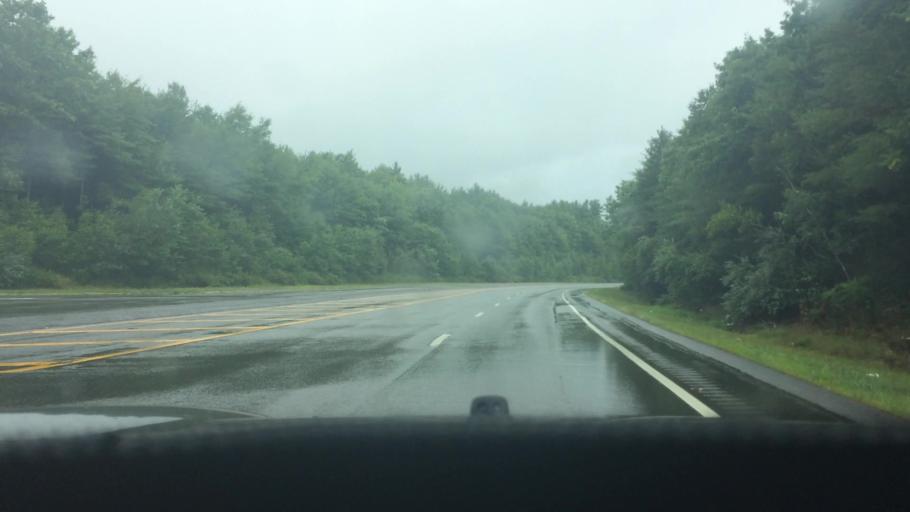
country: US
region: Massachusetts
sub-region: Worcester County
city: Westminster
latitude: 42.5658
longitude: -71.9443
